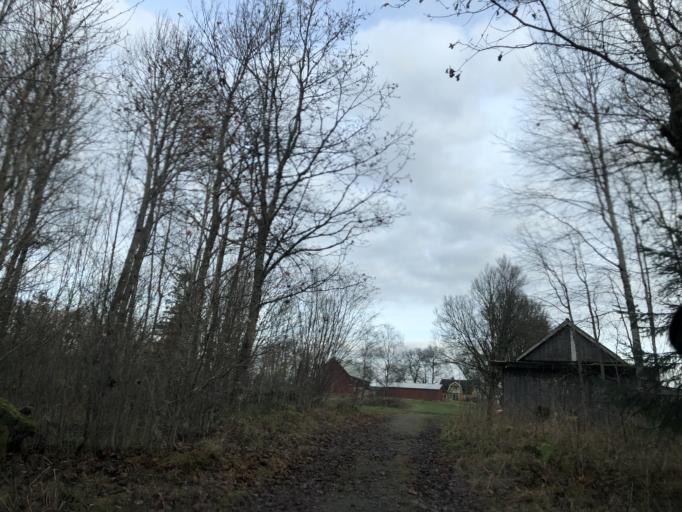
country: SE
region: Vaestra Goetaland
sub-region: Ulricehamns Kommun
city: Ulricehamn
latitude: 57.7234
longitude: 13.3087
